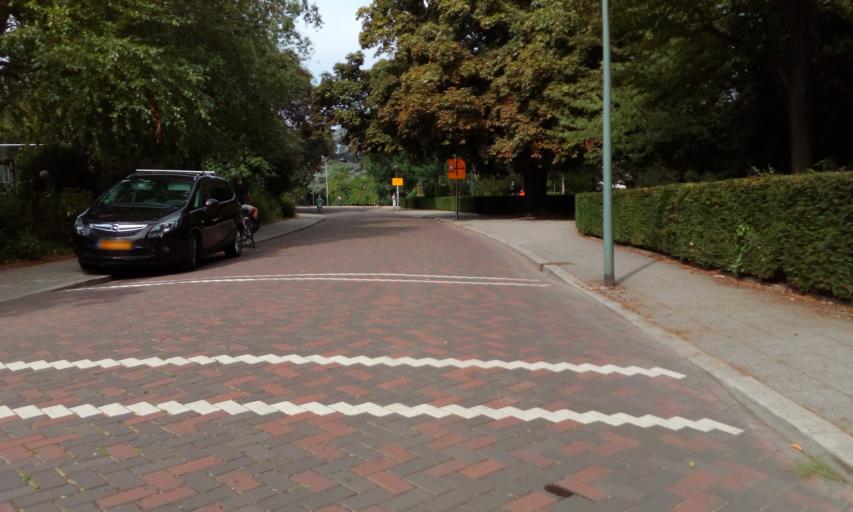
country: NL
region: South Holland
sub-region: Gemeente Schiedam
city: Schiedam
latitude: 51.9095
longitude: 4.3892
